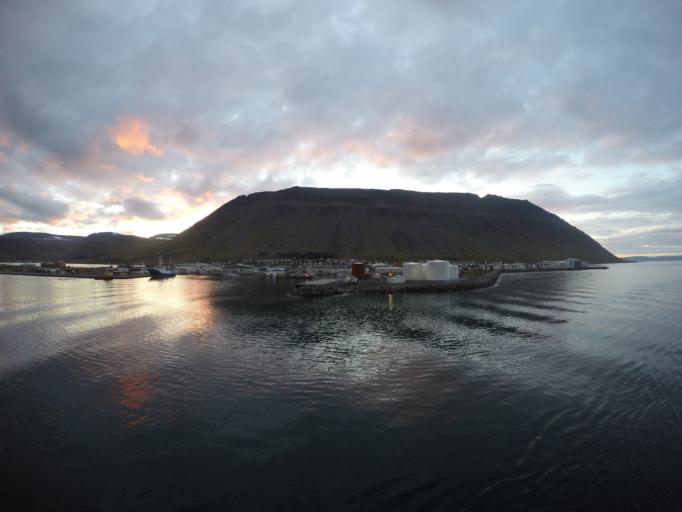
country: IS
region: Westfjords
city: Isafjoerdur
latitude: 66.0672
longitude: -23.1134
